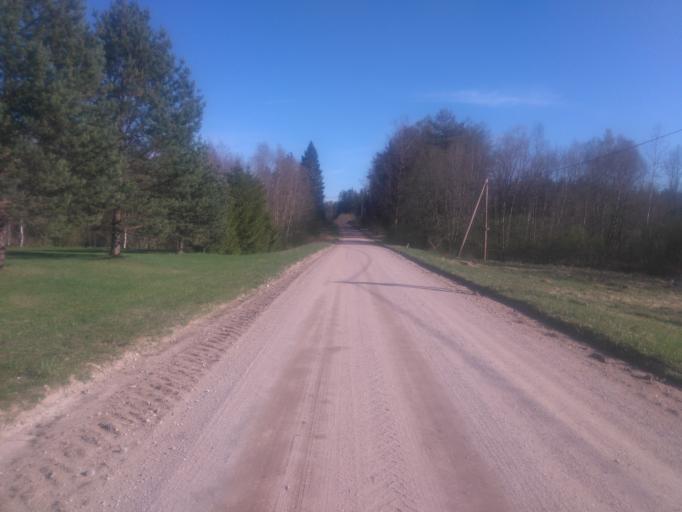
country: LV
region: Vecpiebalga
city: Vecpiebalga
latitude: 57.0157
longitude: 25.8358
